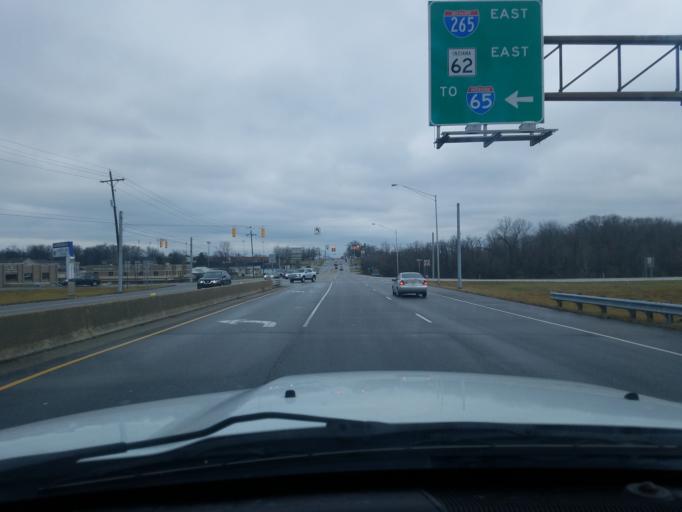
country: US
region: Indiana
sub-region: Floyd County
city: New Albany
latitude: 38.3357
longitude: -85.8180
